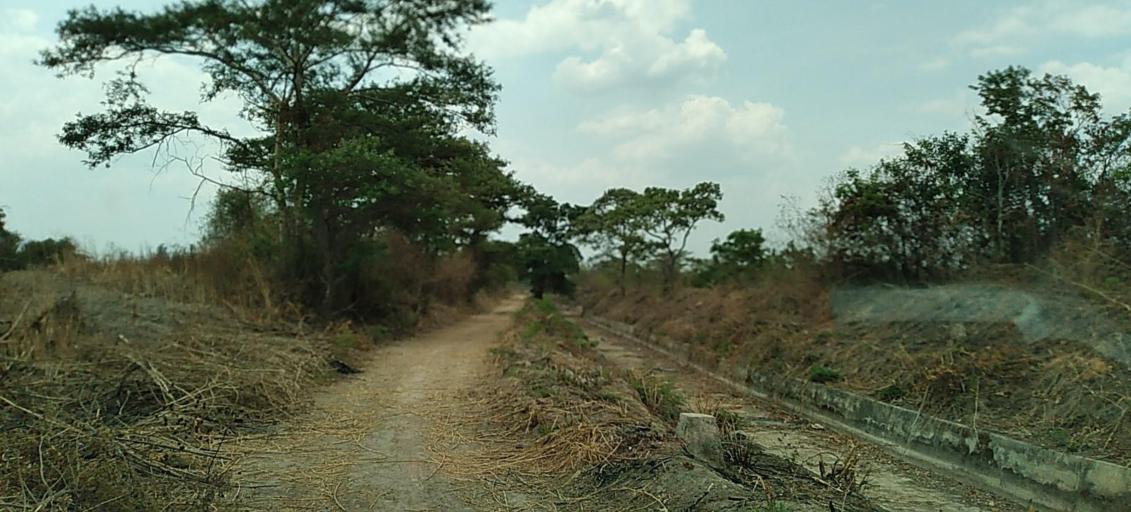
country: ZM
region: Copperbelt
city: Chililabombwe
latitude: -12.3566
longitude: 27.8043
